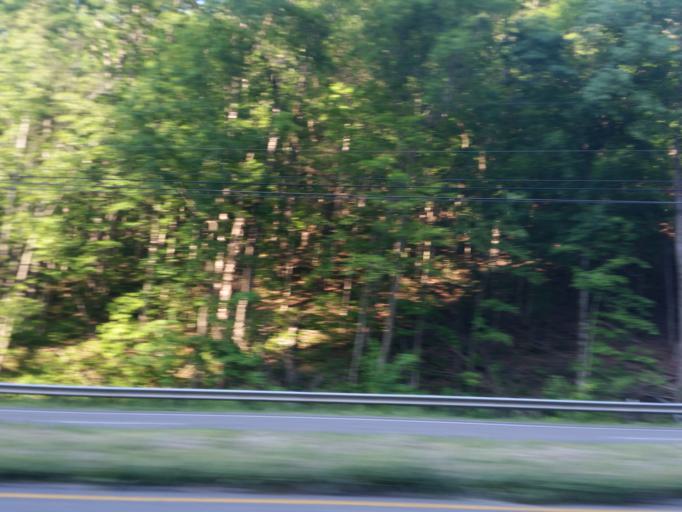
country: US
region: Virginia
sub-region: Washington County
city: Abingdon
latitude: 36.7687
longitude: -82.0682
